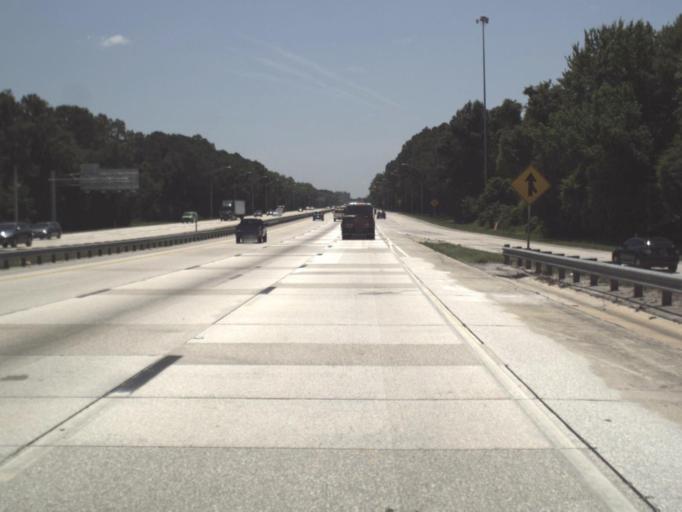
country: US
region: Florida
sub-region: Saint Johns County
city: Fruit Cove
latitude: 30.2189
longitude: -81.5702
